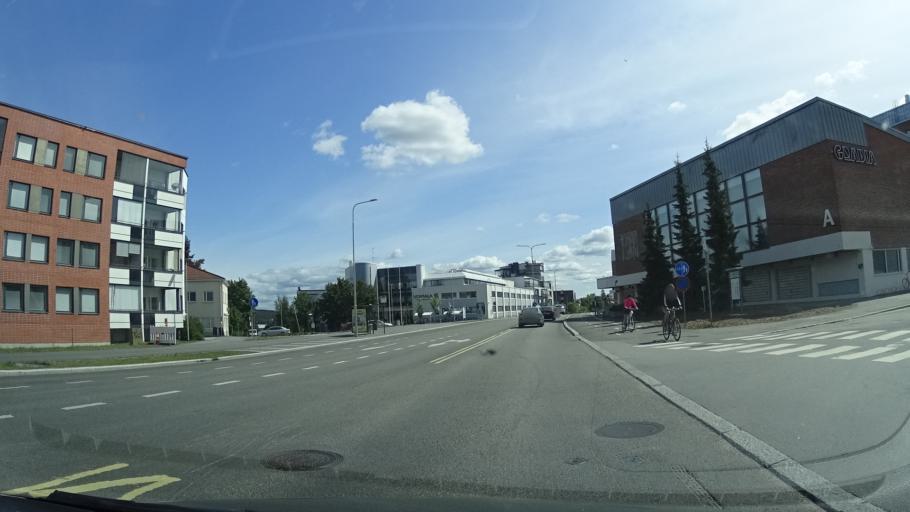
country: FI
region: Central Finland
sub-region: Jyvaeskylae
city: Jyvaeskylae
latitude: 62.2481
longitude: 25.7397
